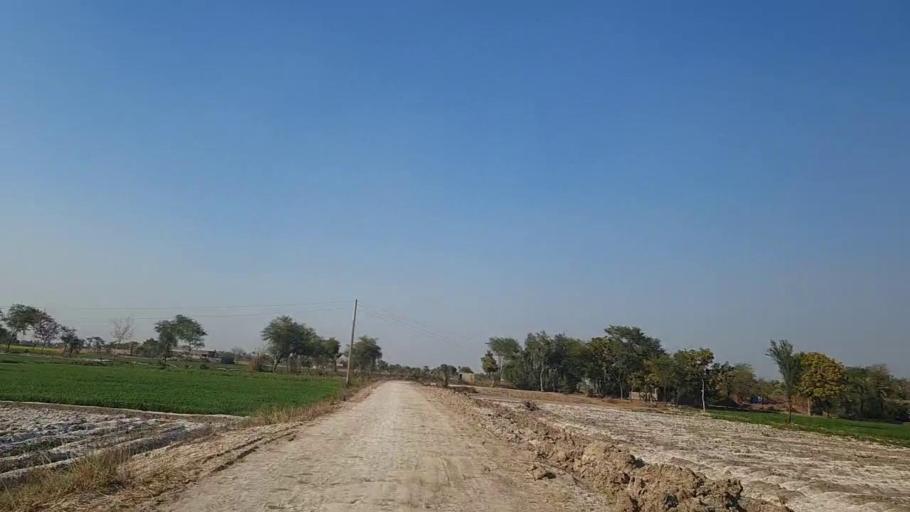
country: PK
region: Sindh
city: Daur
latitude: 26.3258
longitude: 68.1775
